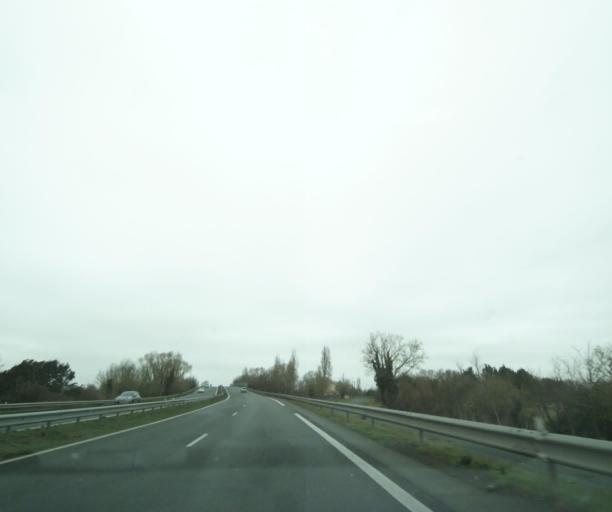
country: FR
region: Poitou-Charentes
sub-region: Departement de la Charente-Maritime
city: Yves
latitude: 46.0386
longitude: -1.0474
